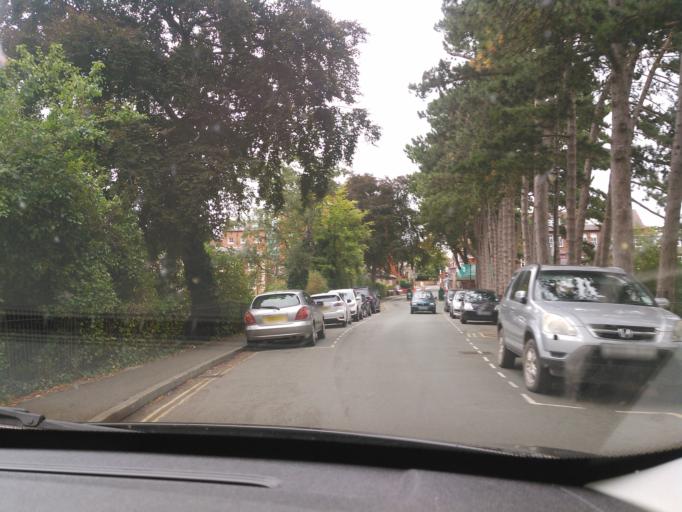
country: GB
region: England
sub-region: Shropshire
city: Shrewsbury
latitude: 52.7047
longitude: -2.7586
